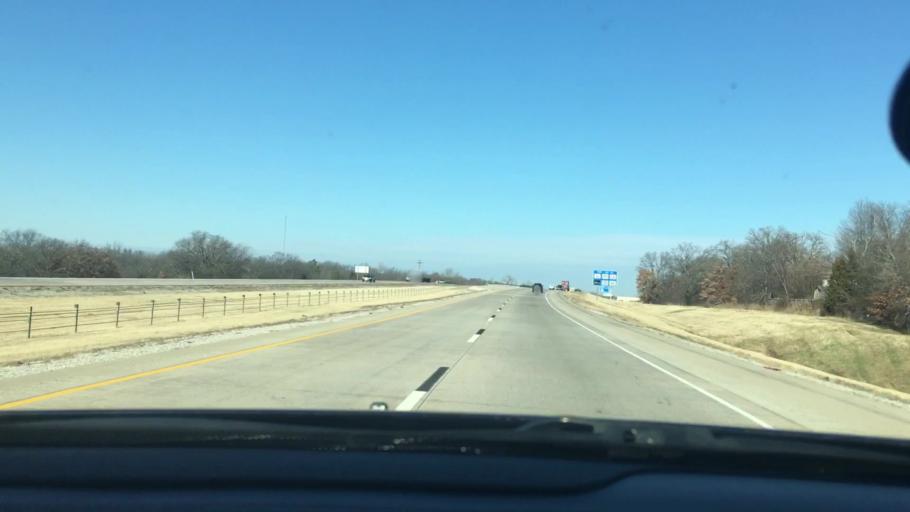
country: US
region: Oklahoma
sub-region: Carter County
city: Ardmore
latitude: 34.1559
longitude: -97.1610
